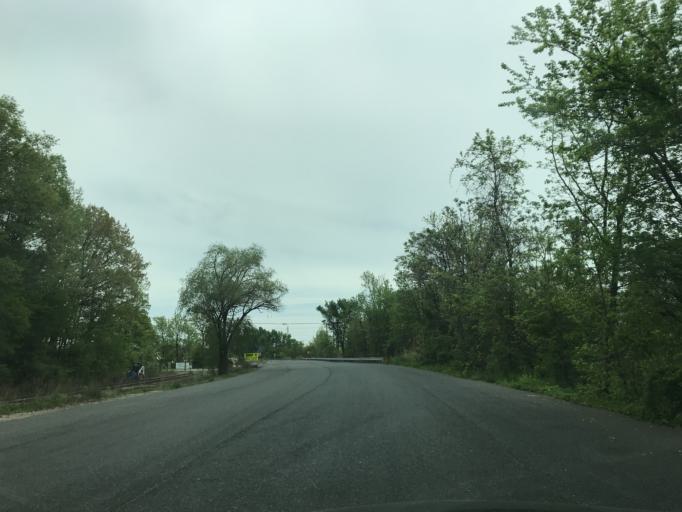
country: US
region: Maryland
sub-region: Baltimore County
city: Edgemere
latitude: 39.2474
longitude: -76.4681
